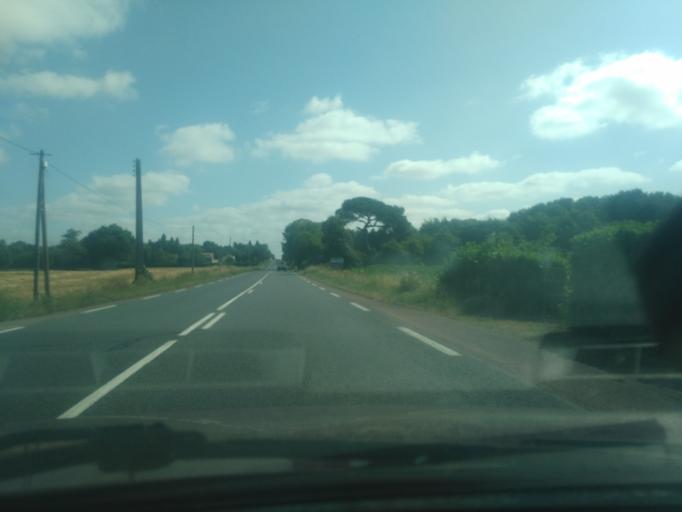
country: FR
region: Pays de la Loire
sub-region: Departement de la Vendee
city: Les Essarts
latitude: 46.7513
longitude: -1.2583
